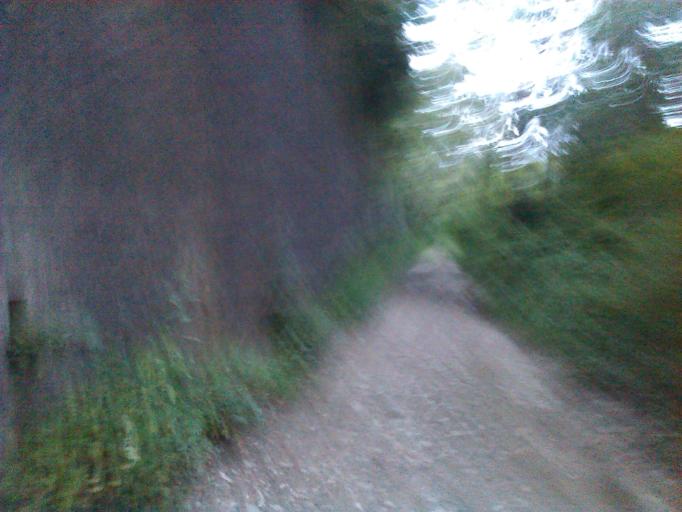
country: IT
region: Tuscany
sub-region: Province of Arezzo
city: Viciomaggio
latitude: 43.4481
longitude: 11.7603
